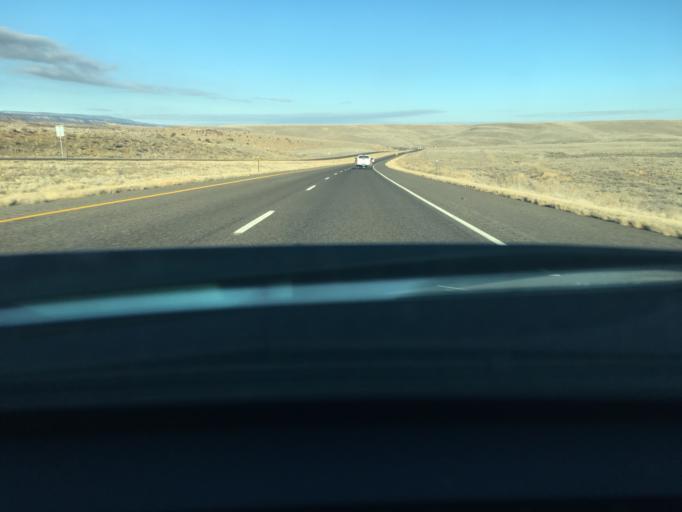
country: US
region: Colorado
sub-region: Delta County
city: Delta
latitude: 38.8037
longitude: -108.2732
